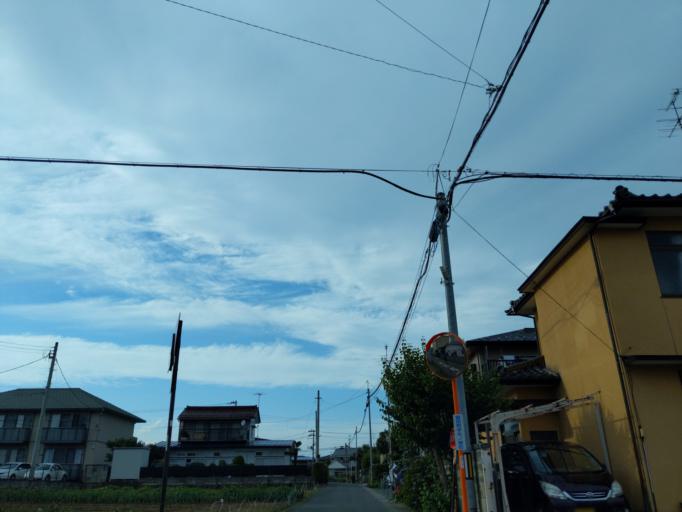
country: JP
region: Fukushima
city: Koriyama
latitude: 37.4138
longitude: 140.3534
